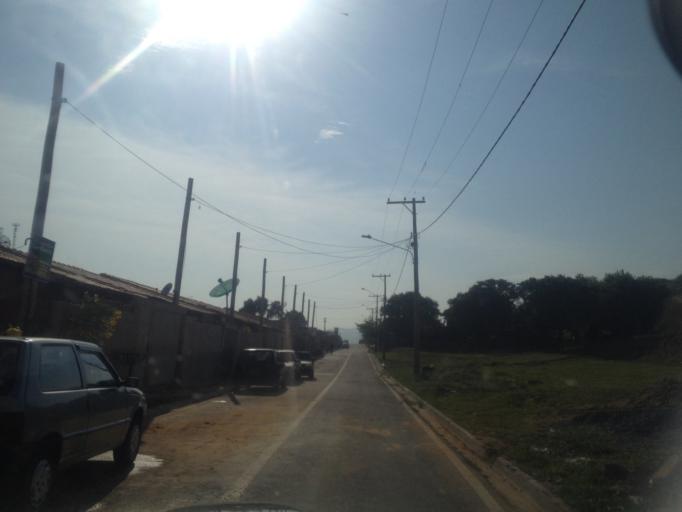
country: BR
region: Rio de Janeiro
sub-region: Porto Real
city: Porto Real
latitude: -22.4411
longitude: -44.3255
